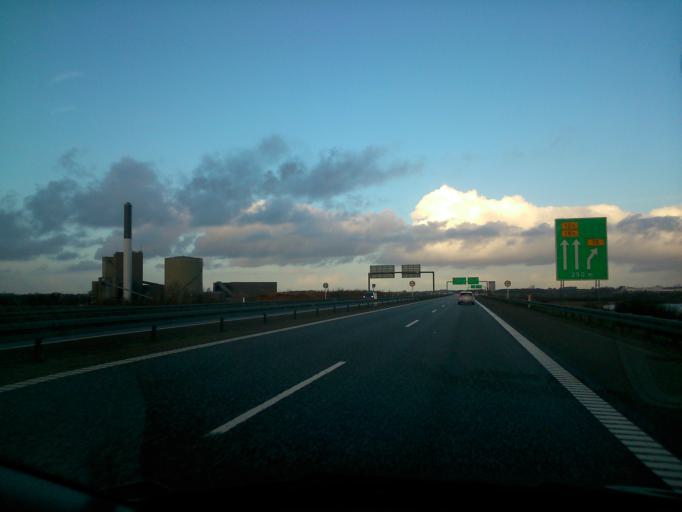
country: DK
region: Central Jutland
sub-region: Herning Kommune
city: Lind
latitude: 56.1167
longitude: 9.0113
